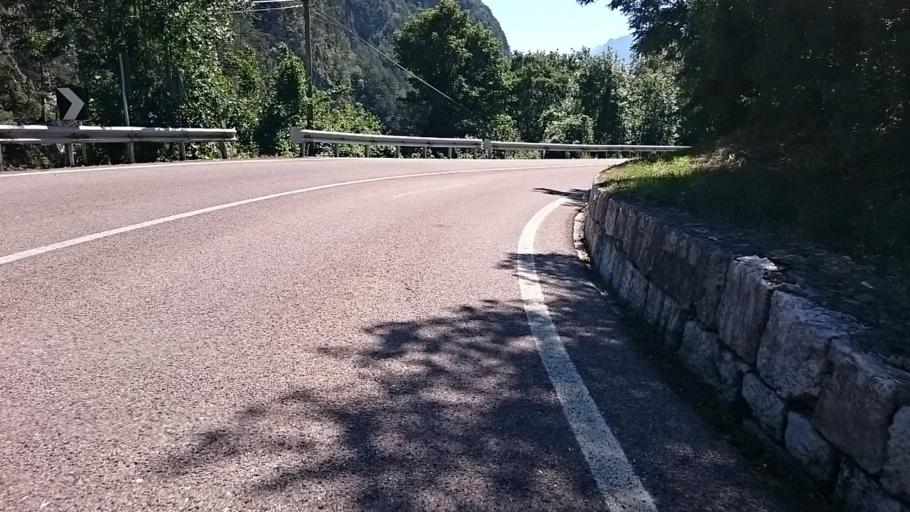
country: IT
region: Veneto
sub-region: Provincia di Belluno
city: Perarolo di Cadore
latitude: 46.3687
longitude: 12.3543
